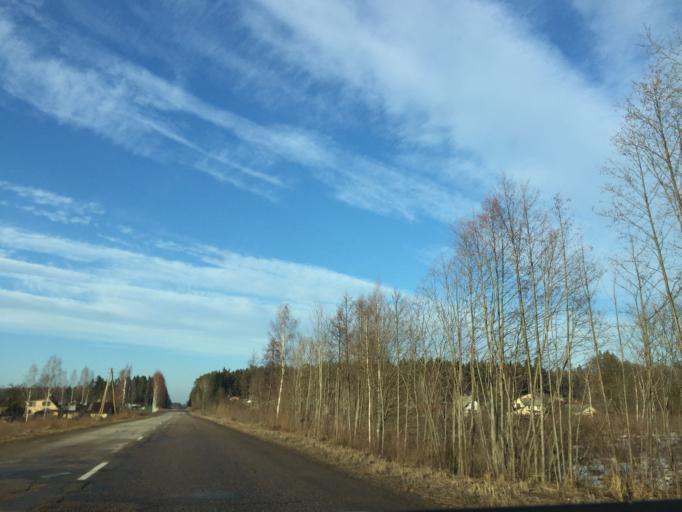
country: LV
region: Lecava
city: Iecava
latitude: 56.7145
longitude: 24.1121
